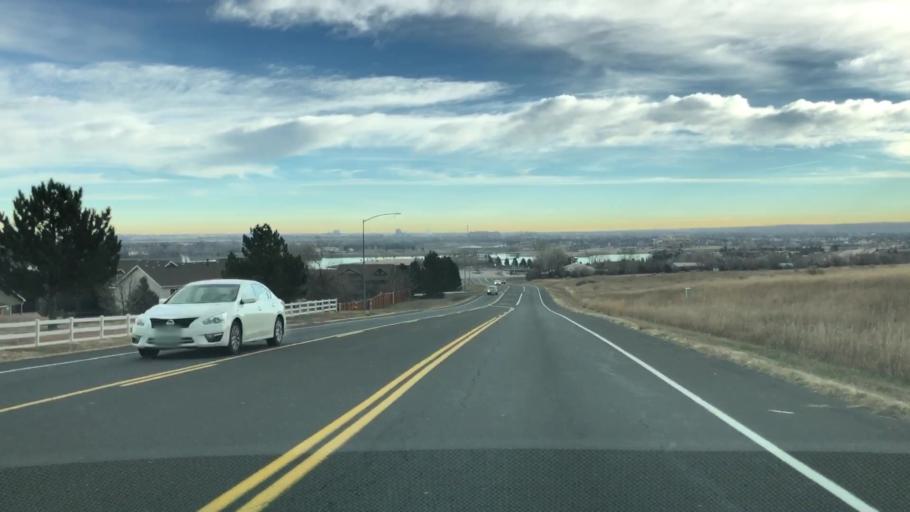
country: US
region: Colorado
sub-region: Weld County
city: Windsor
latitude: 40.4507
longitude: -104.9180
